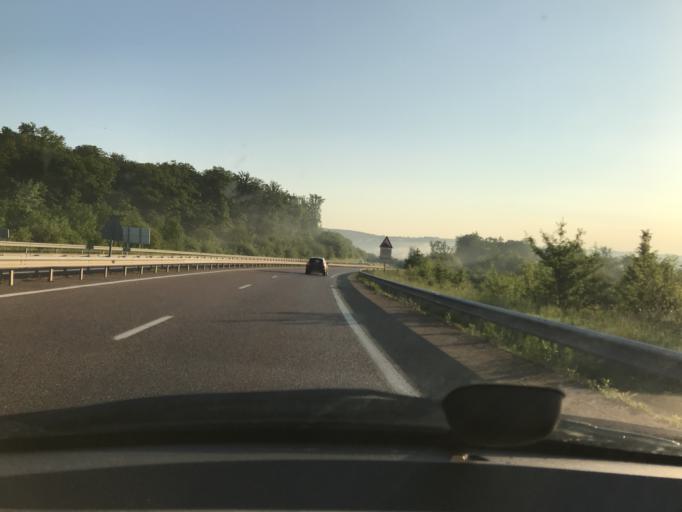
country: DE
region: Saarland
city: Kleinblittersdorf
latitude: 49.1289
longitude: 7.0348
